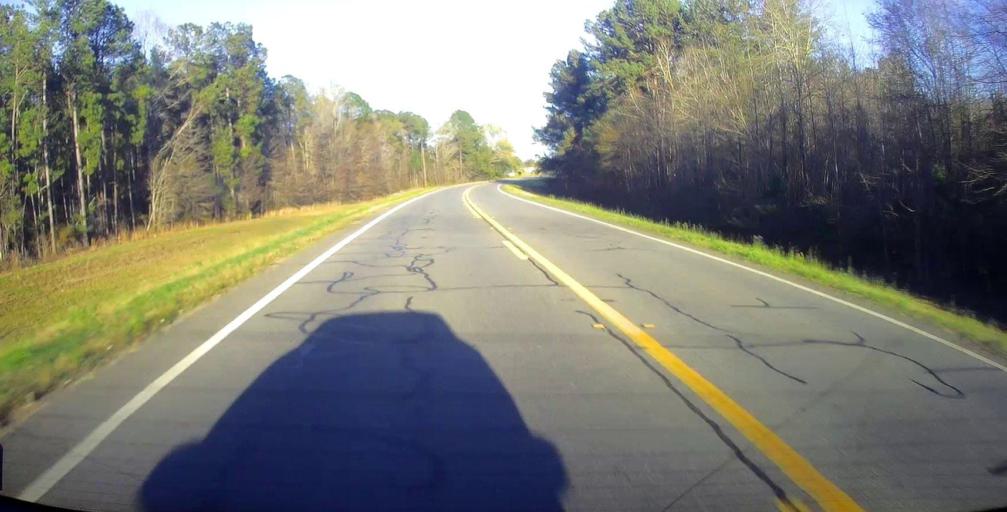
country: US
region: Georgia
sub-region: Wilcox County
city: Abbeville
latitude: 32.0014
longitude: -83.2508
